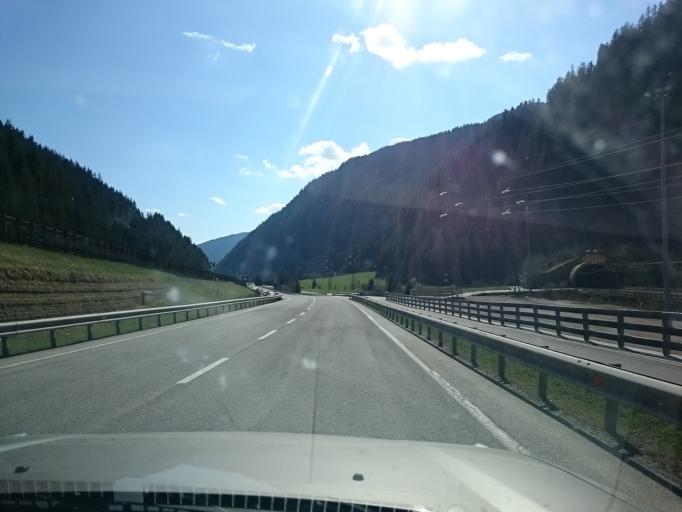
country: IT
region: Trentino-Alto Adige
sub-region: Bolzano
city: Colle Isarco
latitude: 46.9745
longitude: 11.4781
